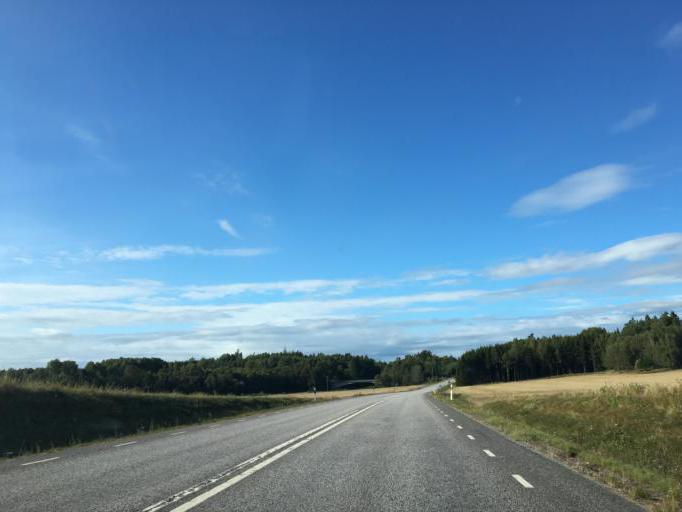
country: SE
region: Soedermanland
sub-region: Nykopings Kommun
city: Nykoping
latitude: 58.8203
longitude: 16.9341
